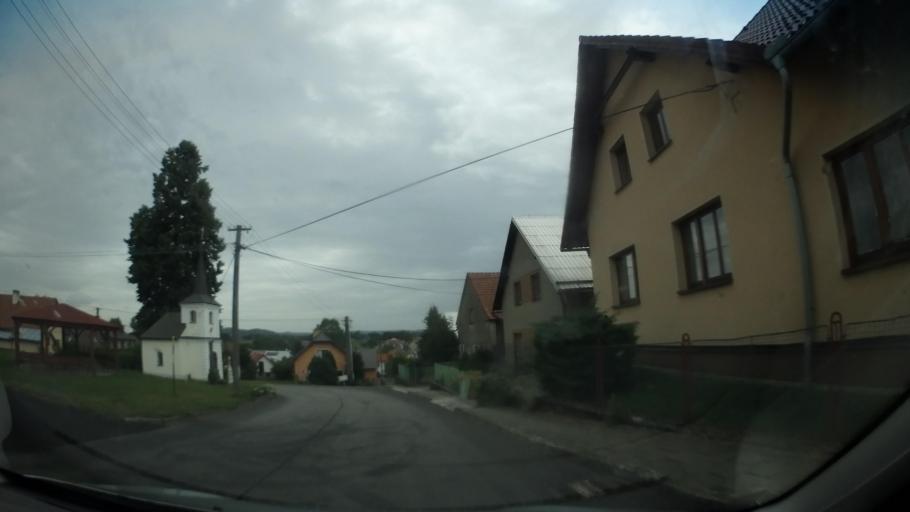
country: CZ
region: Vysocina
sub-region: Okres Zd'ar nad Sazavou
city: Nove Mesto na Morave
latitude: 49.5268
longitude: 16.0373
